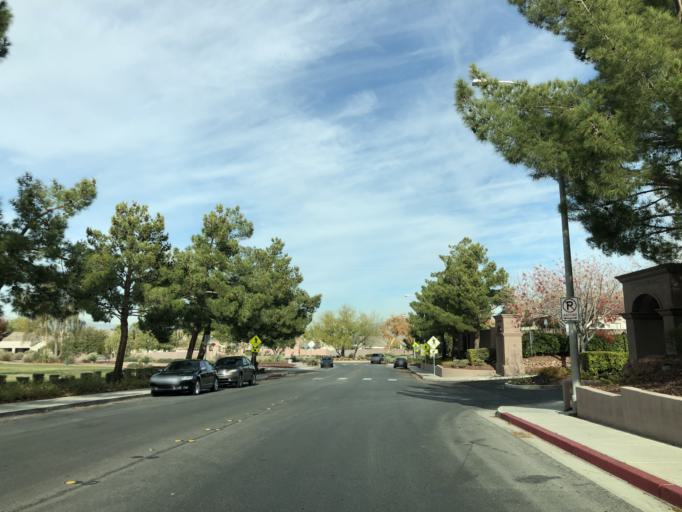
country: US
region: Nevada
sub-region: Clark County
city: Whitney
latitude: 36.0136
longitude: -115.0973
